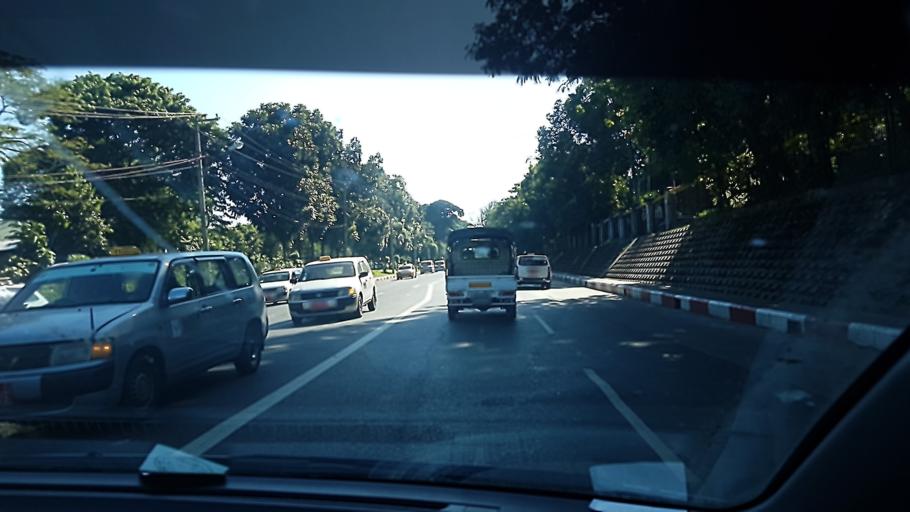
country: MM
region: Yangon
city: Yangon
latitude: 16.8346
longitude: 96.1337
